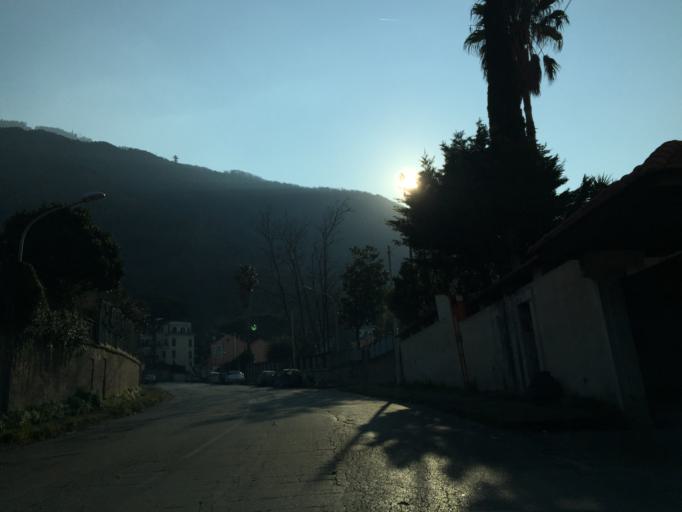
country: IT
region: Campania
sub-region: Provincia di Napoli
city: Castellammare di Stabia
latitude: 40.6885
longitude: 14.4868
